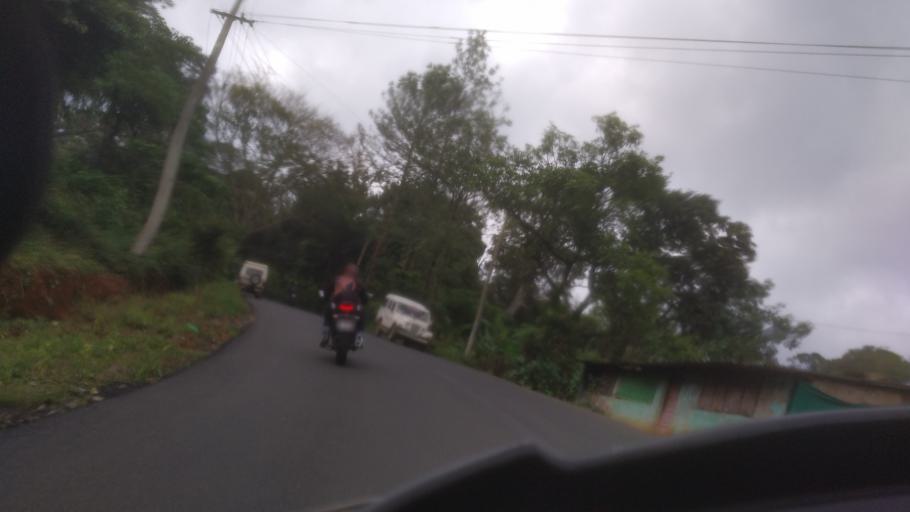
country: IN
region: Tamil Nadu
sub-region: Theni
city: Kombai
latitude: 9.8904
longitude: 77.1503
